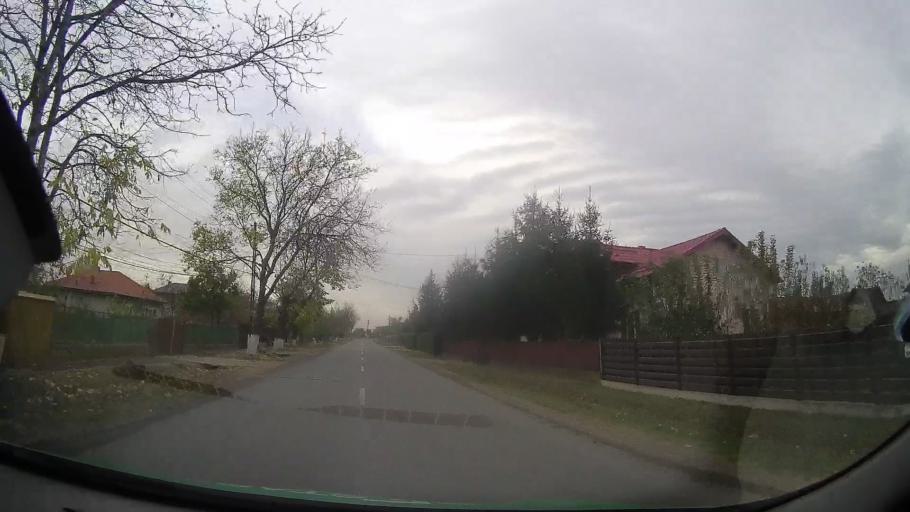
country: RO
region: Prahova
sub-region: Comuna Valea Calugareasca
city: Pantazi
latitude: 44.9143
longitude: 26.1579
